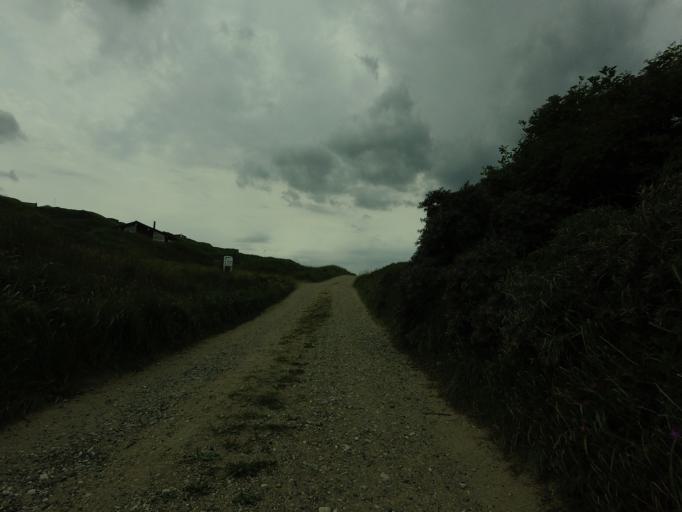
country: DK
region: North Denmark
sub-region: Jammerbugt Kommune
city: Pandrup
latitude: 57.3100
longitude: 9.6481
